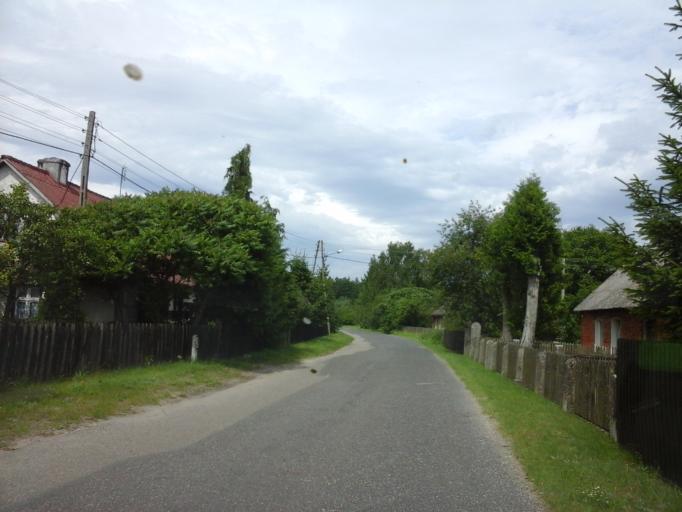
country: PL
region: Lubusz
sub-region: Powiat strzelecko-drezdenecki
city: Dobiegniew
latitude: 53.0894
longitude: 15.7830
